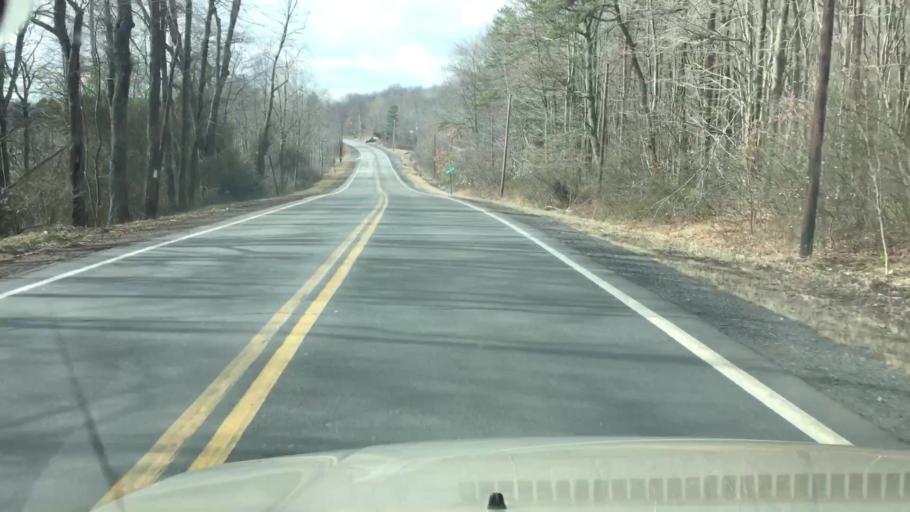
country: US
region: Pennsylvania
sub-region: Luzerne County
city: Oakdale
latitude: 40.9877
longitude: -75.9379
